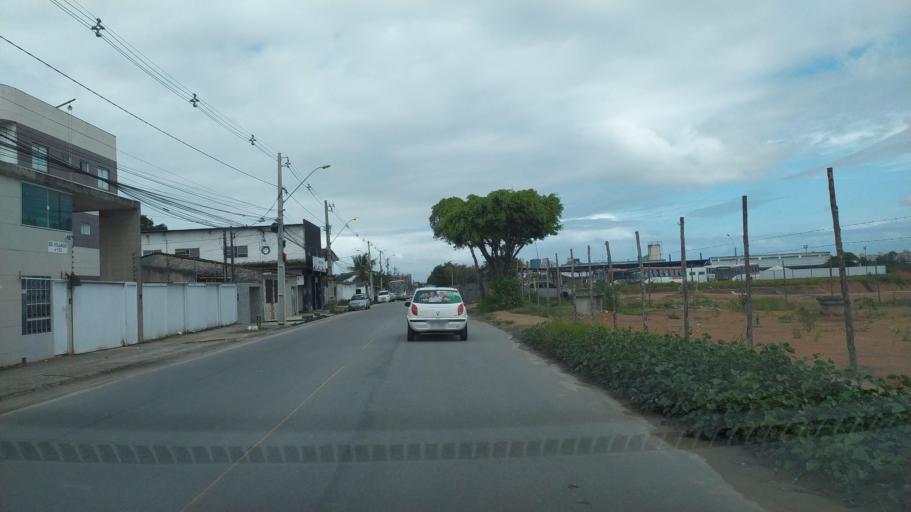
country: BR
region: Alagoas
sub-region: Satuba
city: Satuba
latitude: -9.5462
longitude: -35.7616
